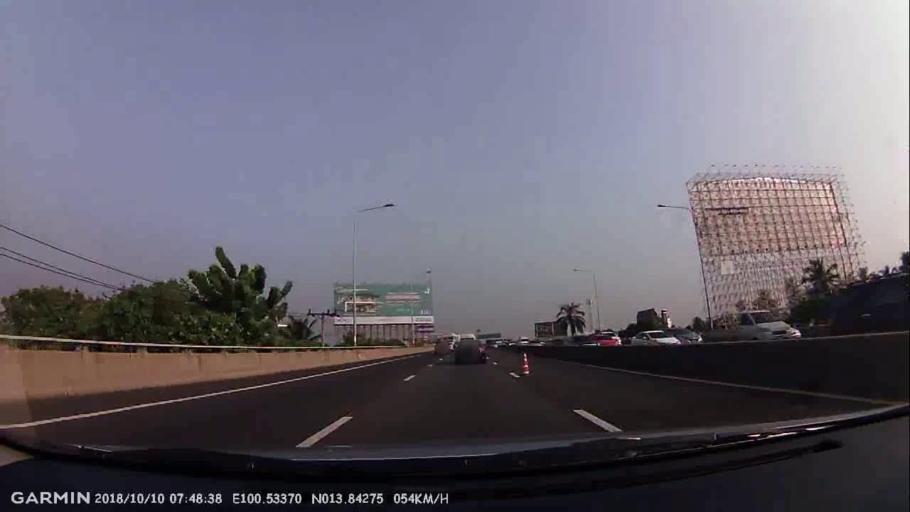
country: TH
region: Nonthaburi
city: Mueang Nonthaburi
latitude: 13.8429
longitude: 100.5336
